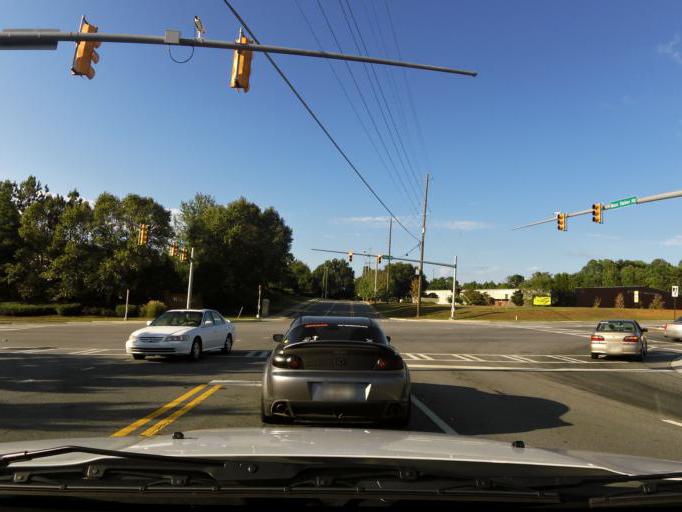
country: US
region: Georgia
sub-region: Cobb County
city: Kennesaw
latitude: 34.0483
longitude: -84.6160
